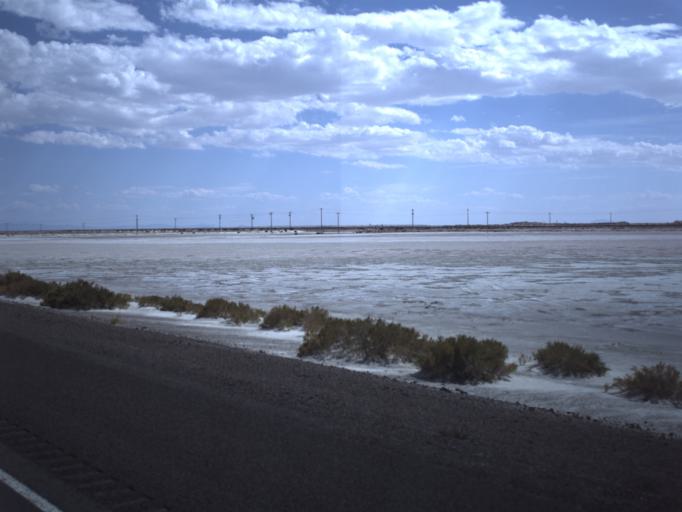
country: US
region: Utah
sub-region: Tooele County
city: Wendover
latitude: 40.7380
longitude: -113.8271
